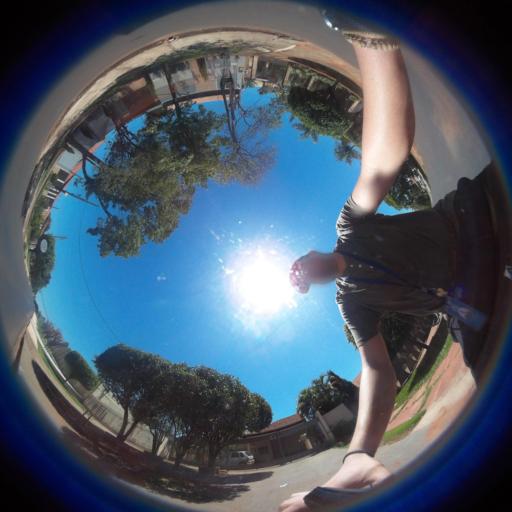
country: BR
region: Mato Grosso do Sul
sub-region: Ponta Pora
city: Ponta Pora
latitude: -22.5280
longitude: -55.7305
